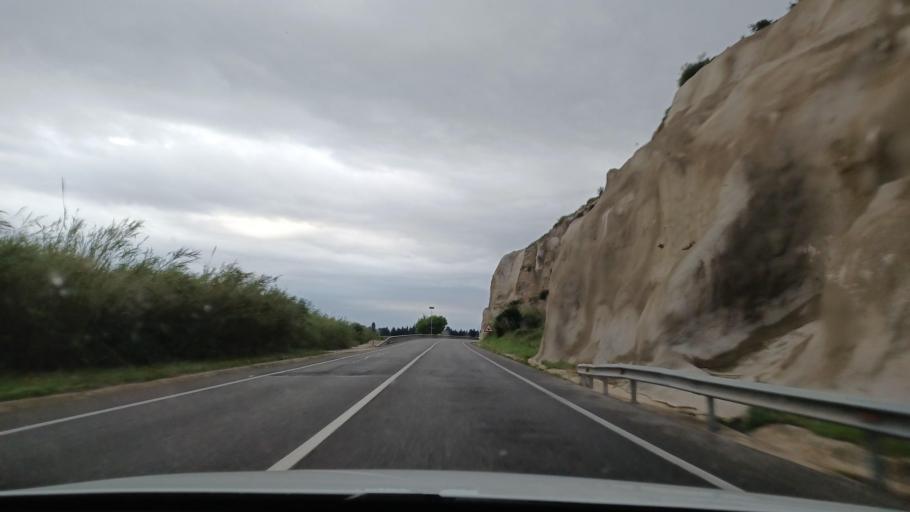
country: ES
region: Catalonia
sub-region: Provincia de Tarragona
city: Tortosa
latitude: 40.7864
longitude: 0.4996
